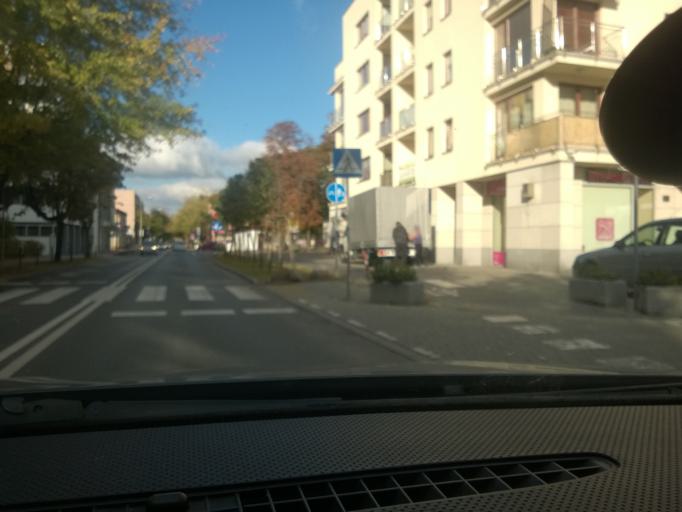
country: PL
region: Masovian Voivodeship
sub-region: Powiat pruszkowski
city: Pruszkow
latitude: 52.1611
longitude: 20.8049
